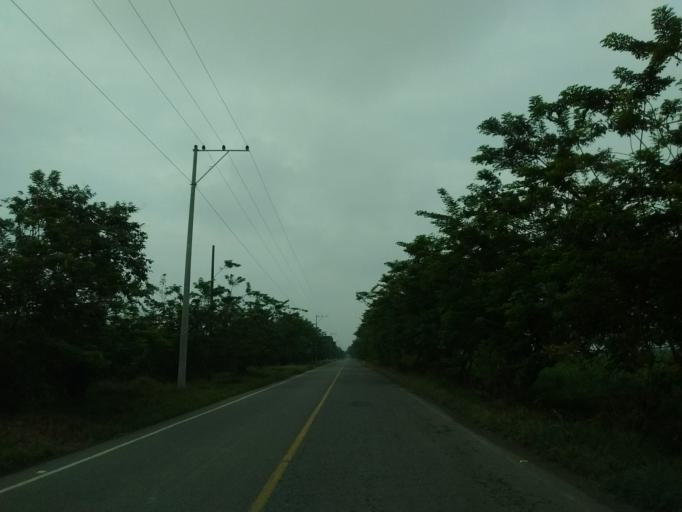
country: CO
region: Cauca
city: Padilla
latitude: 3.2274
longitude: -76.3419
